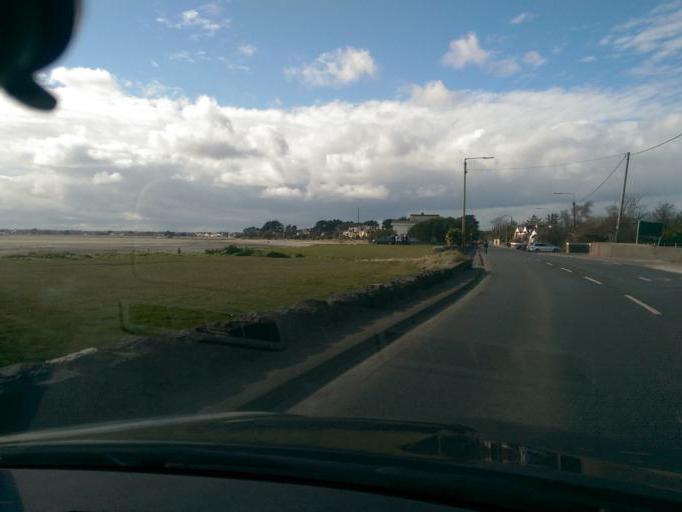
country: IE
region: Leinster
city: Sutton
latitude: 53.3862
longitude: -6.1026
